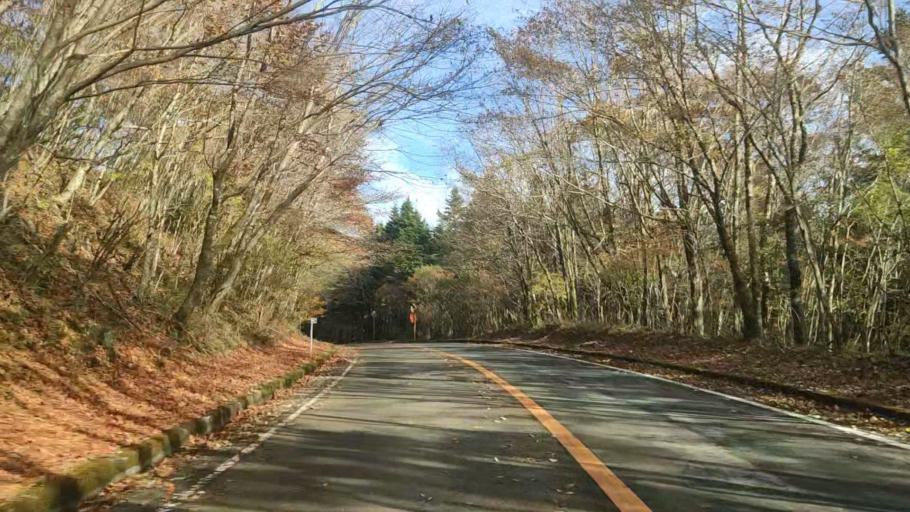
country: JP
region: Shizuoka
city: Fujinomiya
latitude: 35.3027
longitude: 138.7278
